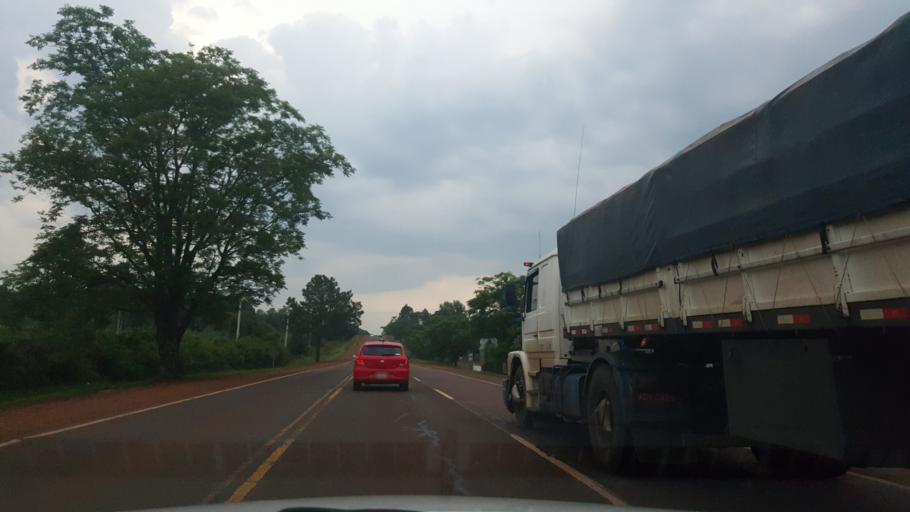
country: AR
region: Misiones
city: Santo Pipo
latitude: -27.1501
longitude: -55.4163
